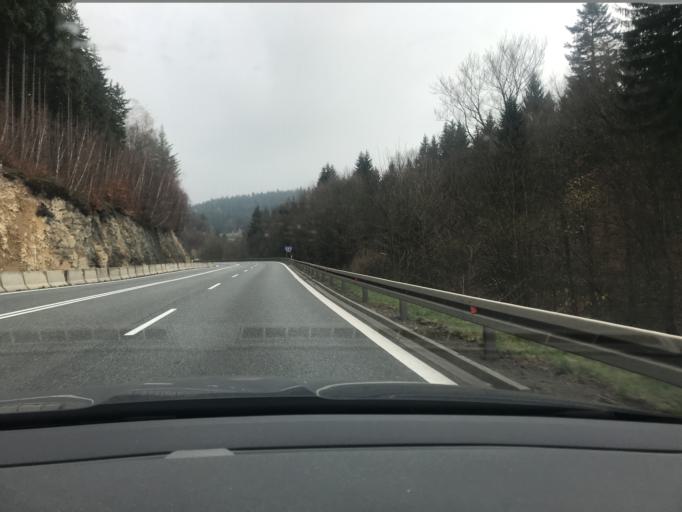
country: PL
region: Lower Silesian Voivodeship
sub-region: Powiat klodzki
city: Lewin Klodzki
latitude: 50.4020
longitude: 16.3379
